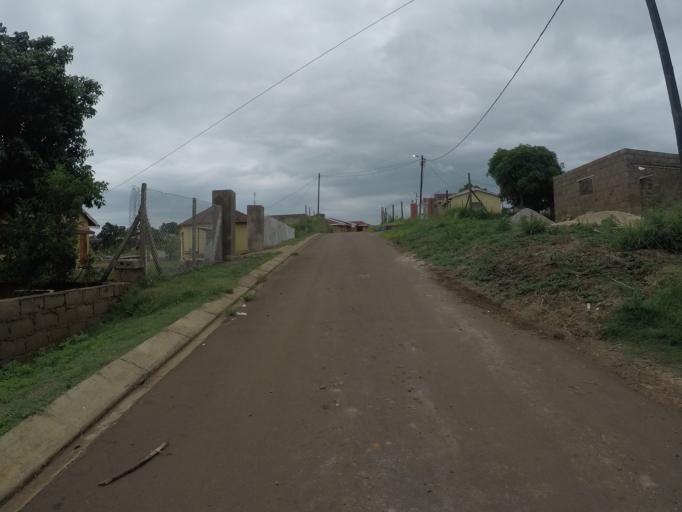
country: ZA
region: KwaZulu-Natal
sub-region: uThungulu District Municipality
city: Empangeni
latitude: -28.7815
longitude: 31.8613
